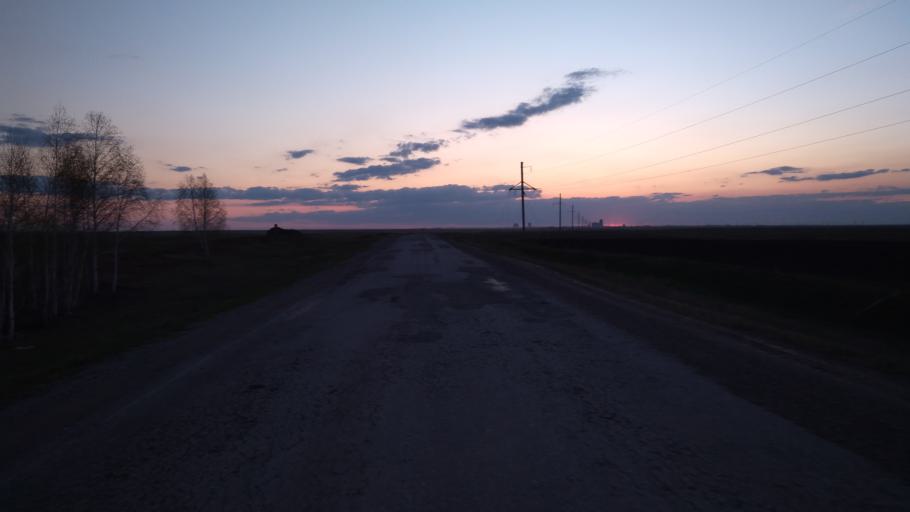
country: RU
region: Chelyabinsk
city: Troitsk
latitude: 54.0864
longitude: 61.6642
